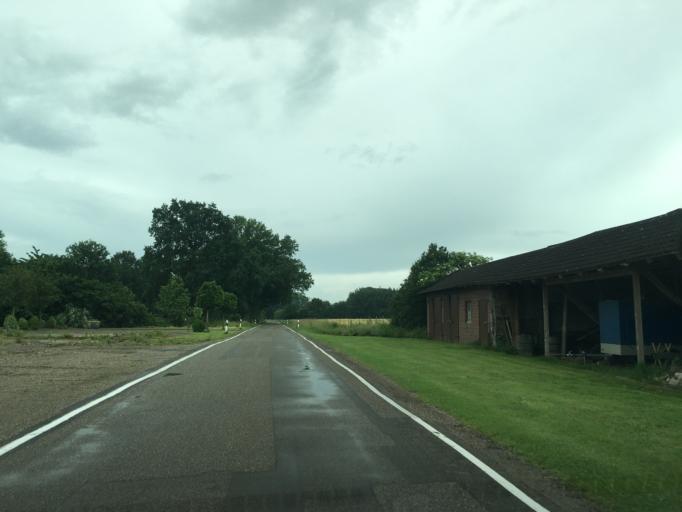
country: DE
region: North Rhine-Westphalia
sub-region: Regierungsbezirk Munster
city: Altenberge
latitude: 52.0193
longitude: 7.4585
